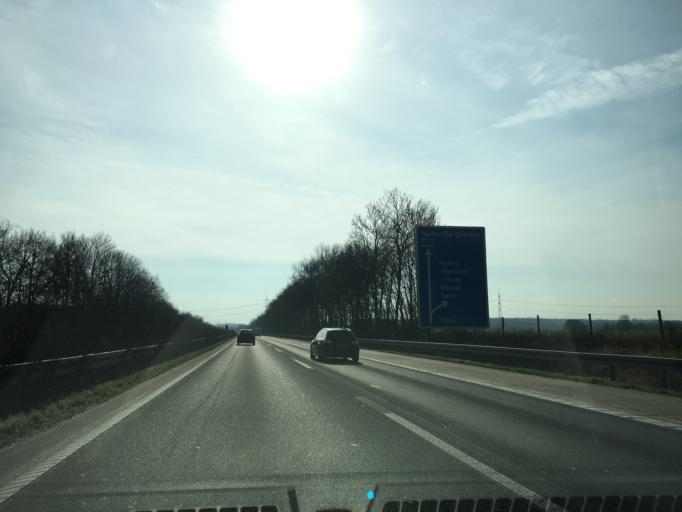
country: DE
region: North Rhine-Westphalia
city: Werne
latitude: 51.7018
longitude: 7.6636
